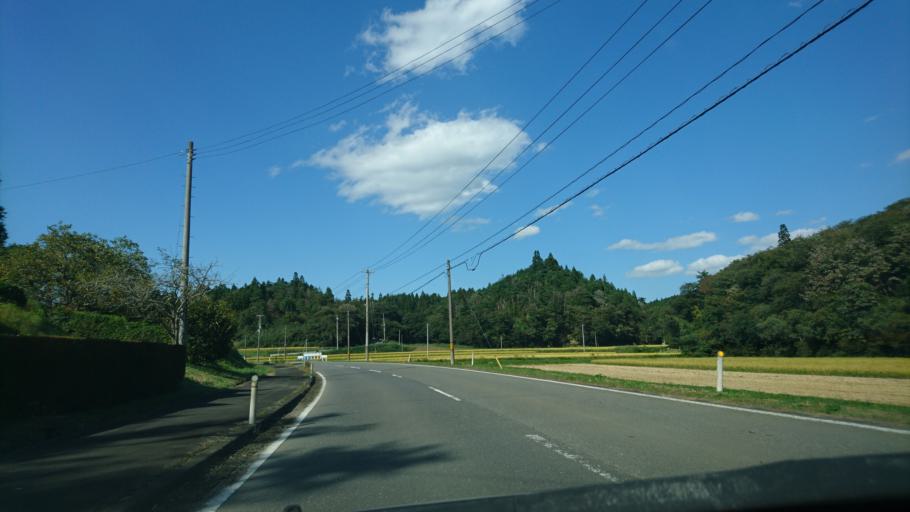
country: JP
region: Iwate
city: Ichinoseki
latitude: 38.8653
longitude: 141.0453
